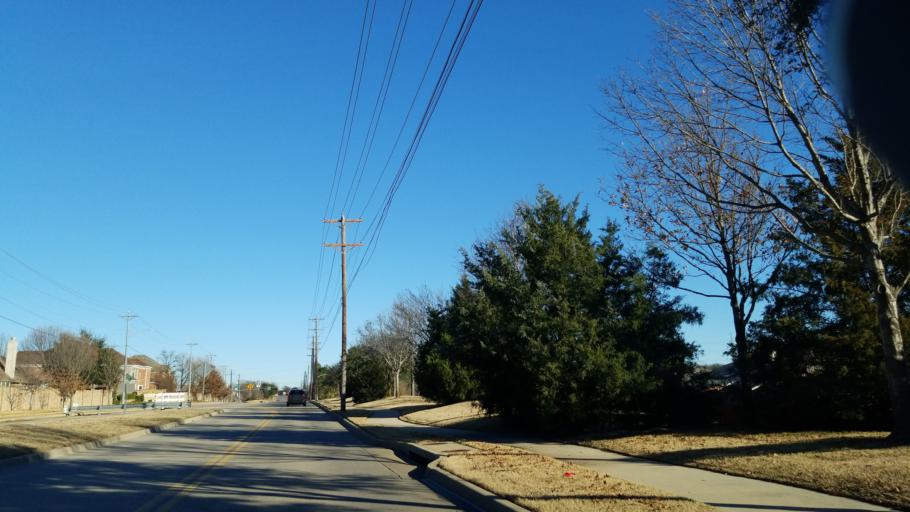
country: US
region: Texas
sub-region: Denton County
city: Corinth
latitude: 33.1583
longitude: -97.0962
